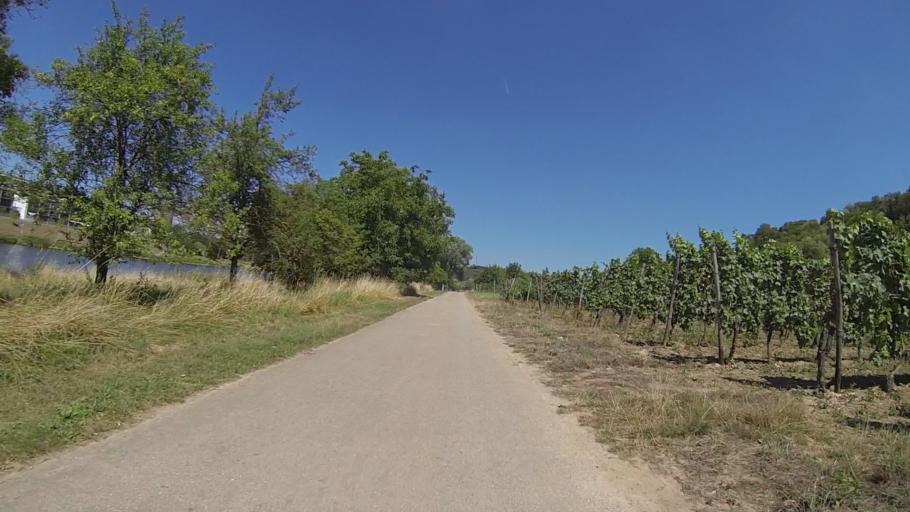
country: LU
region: Grevenmacher
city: Wasserbillig
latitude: 49.7090
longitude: 6.4967
